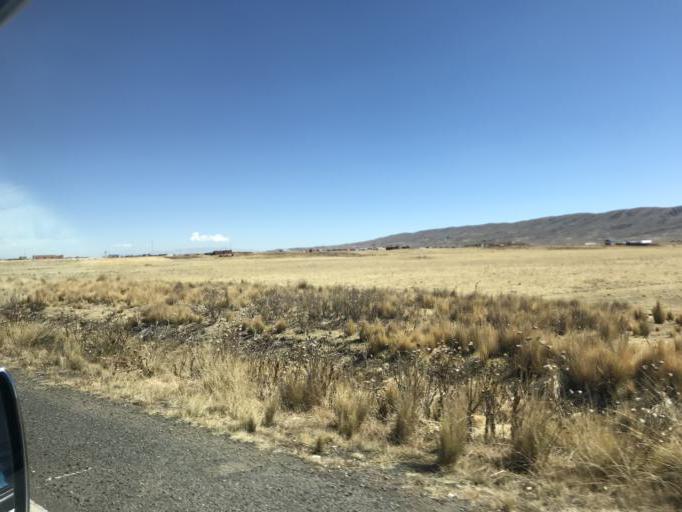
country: BO
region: La Paz
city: Tiahuanaco
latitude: -16.5693
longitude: -68.6631
